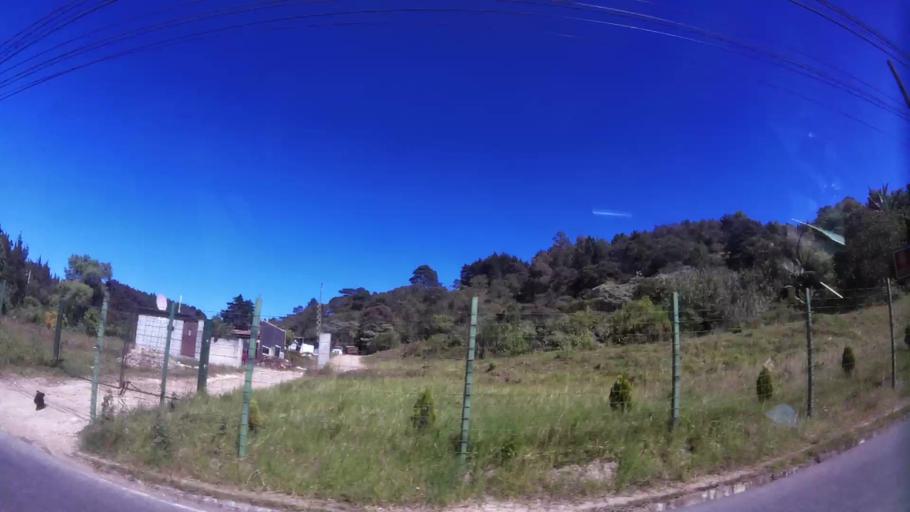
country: GT
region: Guatemala
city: San Jose Pinula
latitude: 14.5188
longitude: -90.4351
